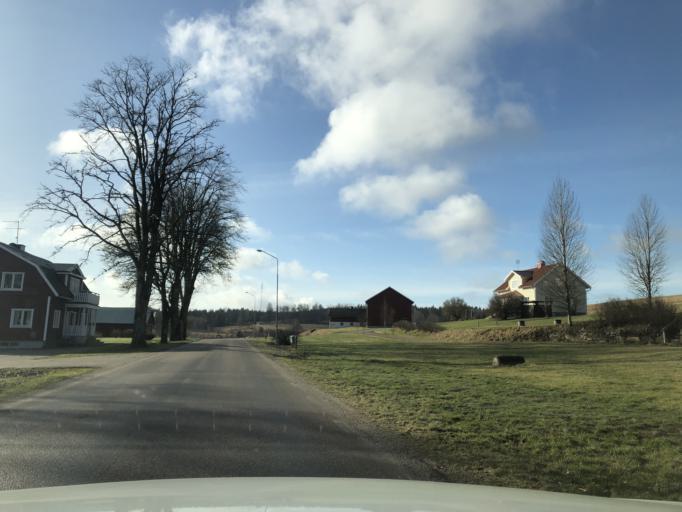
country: SE
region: Vaestra Goetaland
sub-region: Ulricehamns Kommun
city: Ulricehamn
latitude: 57.7998
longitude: 13.5964
